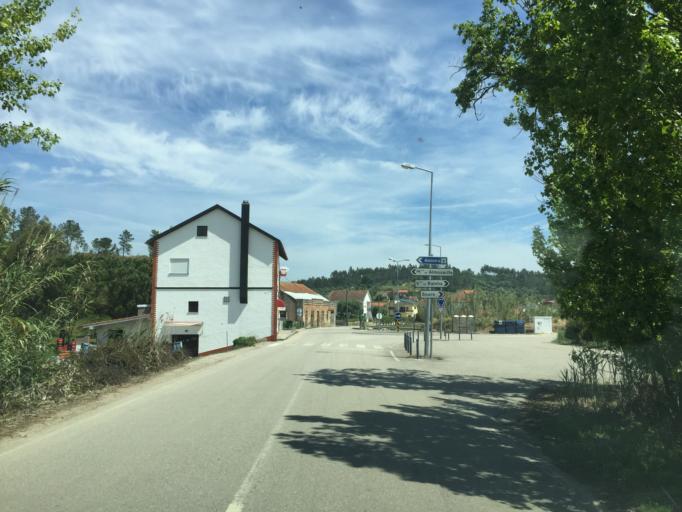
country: PT
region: Leiria
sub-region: Pombal
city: Lourical
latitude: 40.0730
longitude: -8.7367
